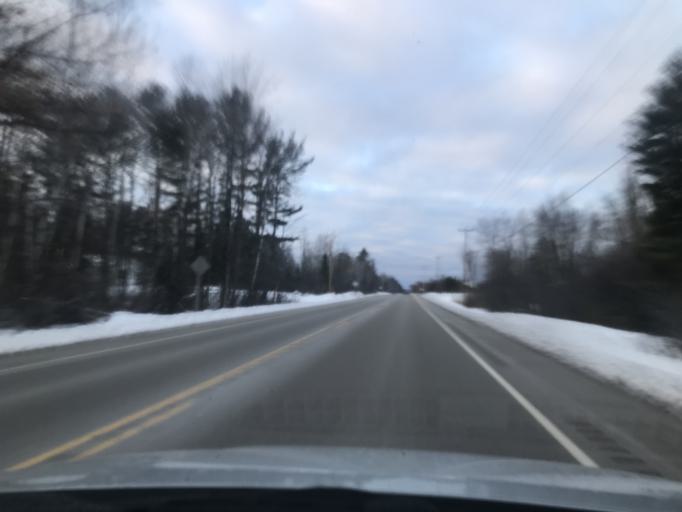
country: US
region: Wisconsin
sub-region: Marinette County
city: Marinette
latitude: 45.1190
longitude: -87.6819
